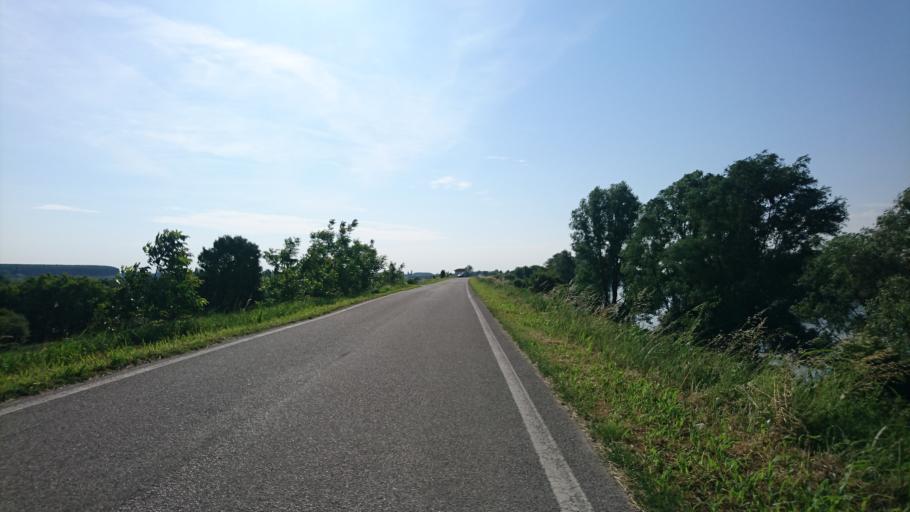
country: IT
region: Veneto
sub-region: Provincia di Verona
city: Villa Bartolomea
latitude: 45.1722
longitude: 11.3437
